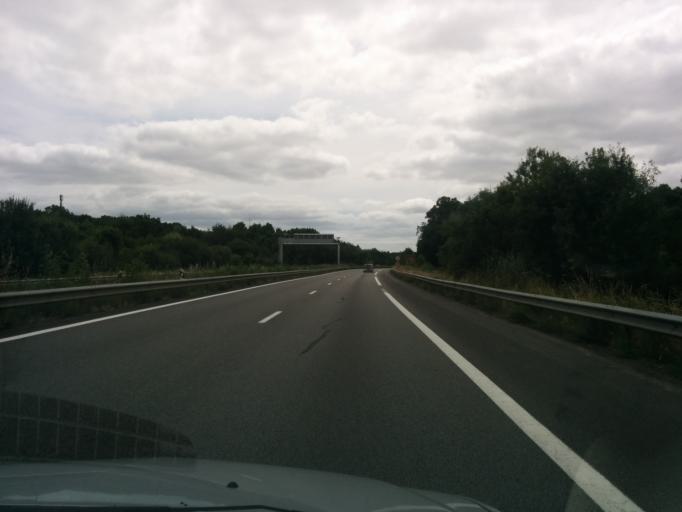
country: FR
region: Pays de la Loire
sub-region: Departement de la Loire-Atlantique
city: Basse-Goulaine
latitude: 47.2130
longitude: -1.4514
